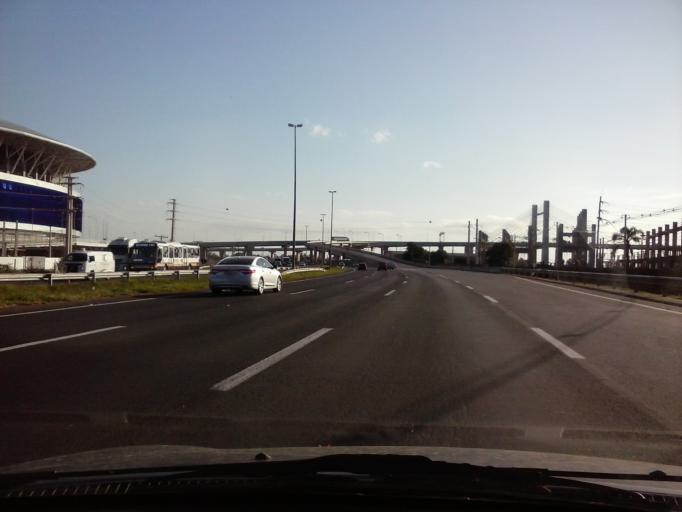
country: BR
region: Rio Grande do Sul
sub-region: Canoas
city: Canoas
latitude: -29.9712
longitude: -51.1935
